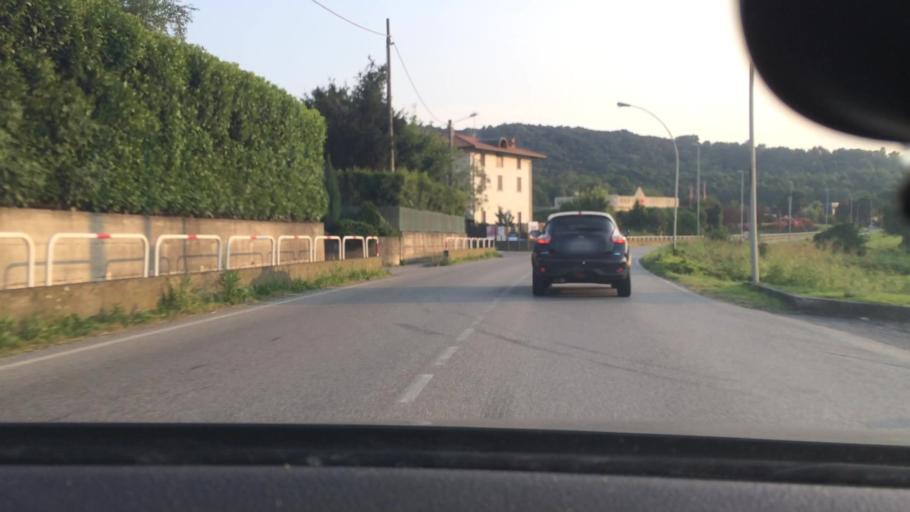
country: IT
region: Lombardy
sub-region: Provincia di Lecco
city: Brivio
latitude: 45.7365
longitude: 9.4356
